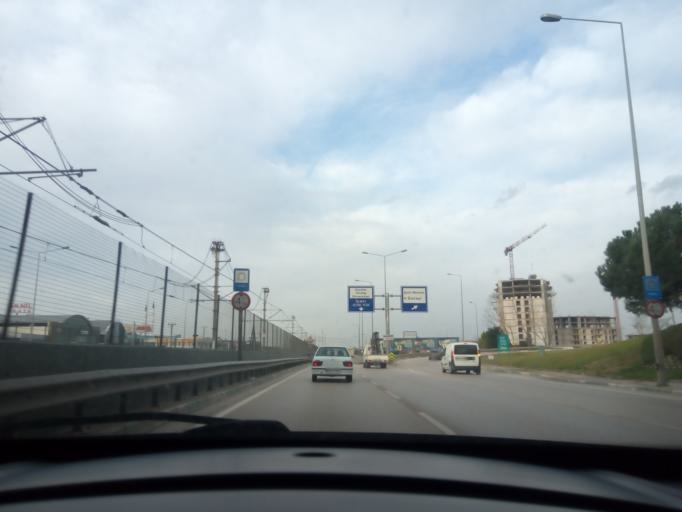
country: TR
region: Bursa
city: Cali
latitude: 40.2121
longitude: 28.9390
